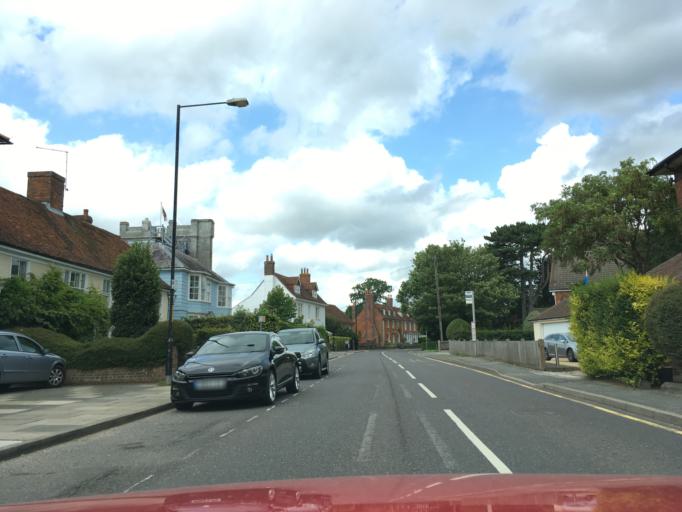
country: GB
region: England
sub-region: Kent
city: Tenterden
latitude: 51.0709
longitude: 0.6905
